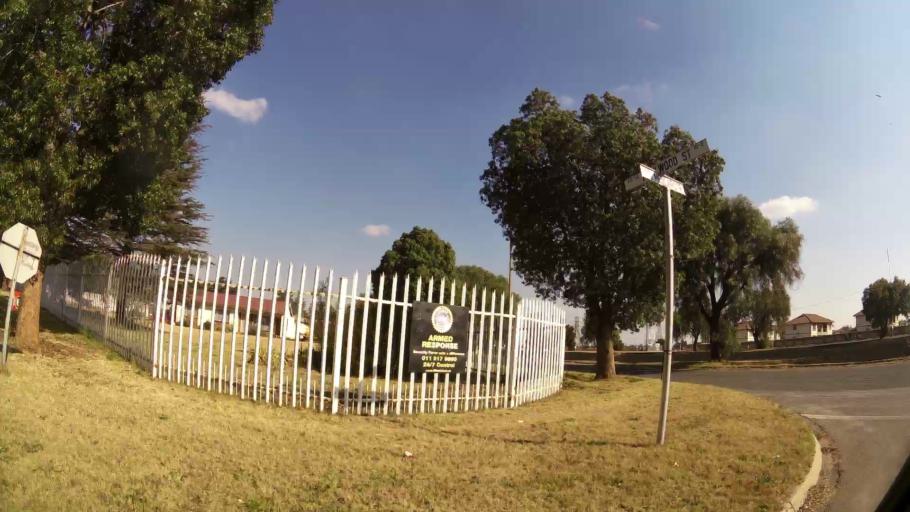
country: ZA
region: Gauteng
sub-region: Ekurhuleni Metropolitan Municipality
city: Boksburg
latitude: -26.2475
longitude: 28.2924
